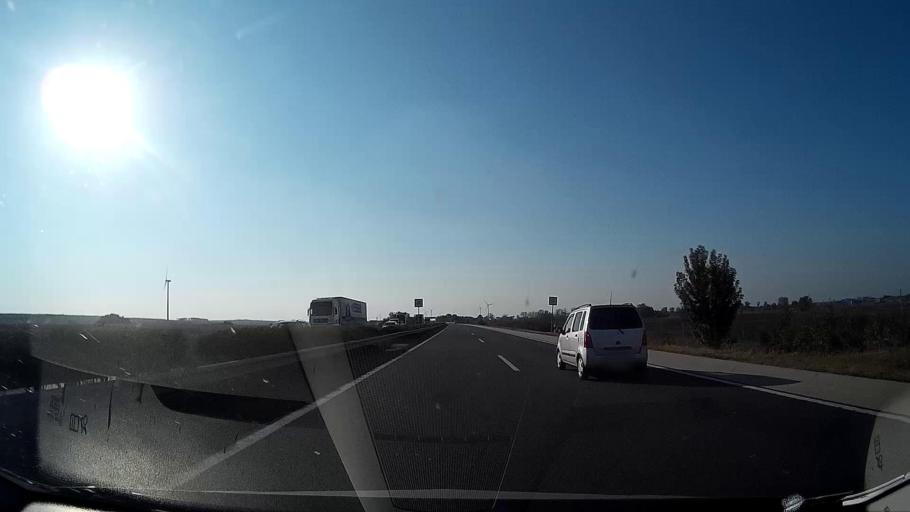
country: HU
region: Komarom-Esztergom
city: Acs
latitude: 47.6828
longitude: 18.0112
